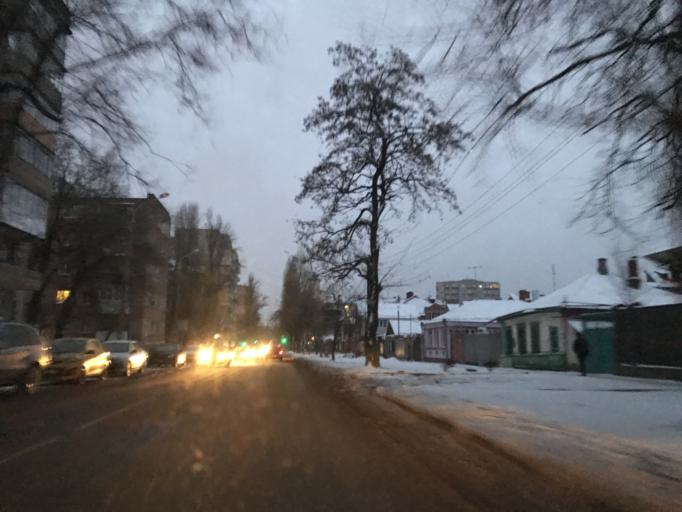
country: RU
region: Rostov
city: Imeni Chkalova
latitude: 47.2492
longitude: 39.7710
